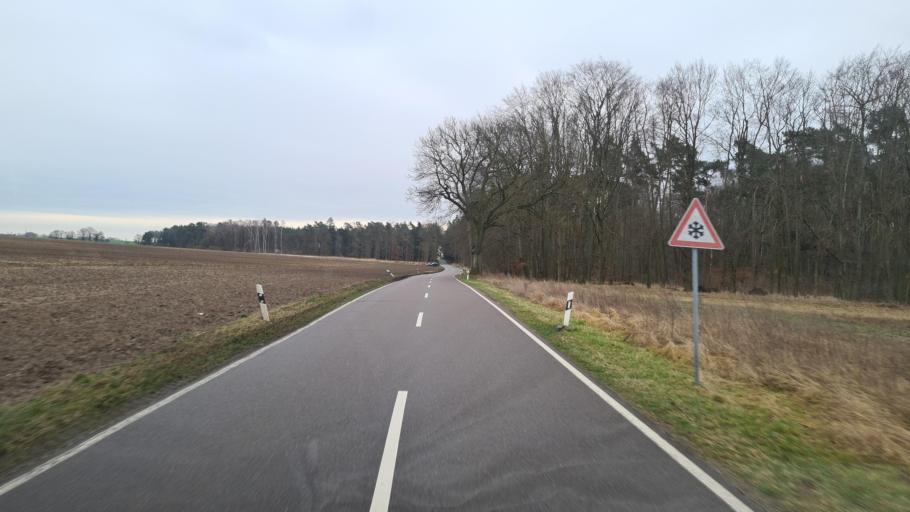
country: DE
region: Brandenburg
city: Gransee
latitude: 52.9381
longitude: 13.2312
